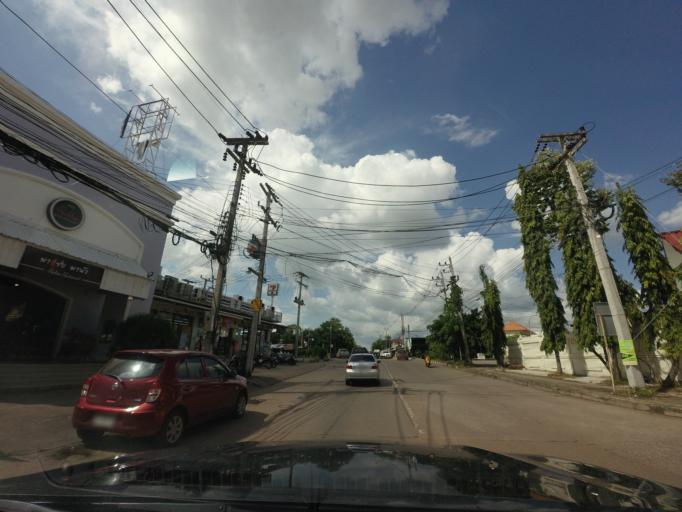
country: TH
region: Changwat Udon Thani
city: Udon Thani
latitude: 17.4148
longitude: 102.7771
